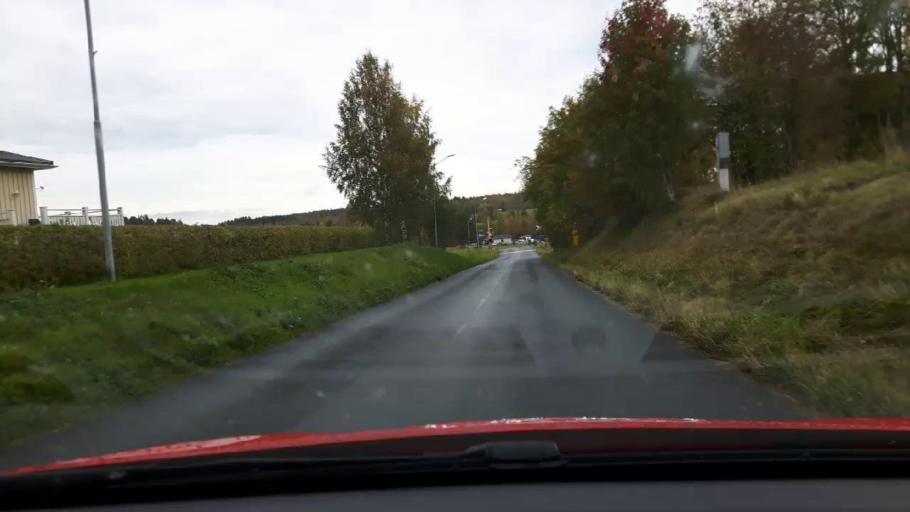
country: SE
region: Jaemtland
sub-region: Bergs Kommun
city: Hoverberg
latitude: 62.9175
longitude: 14.5210
